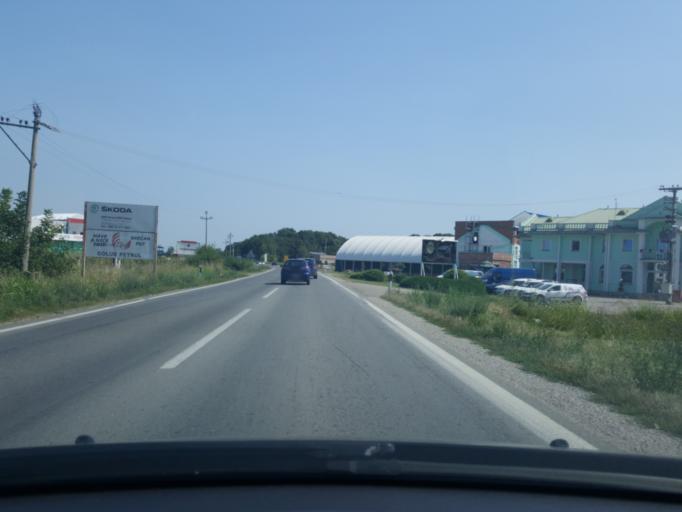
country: RS
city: Majur
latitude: 44.7599
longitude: 19.6442
